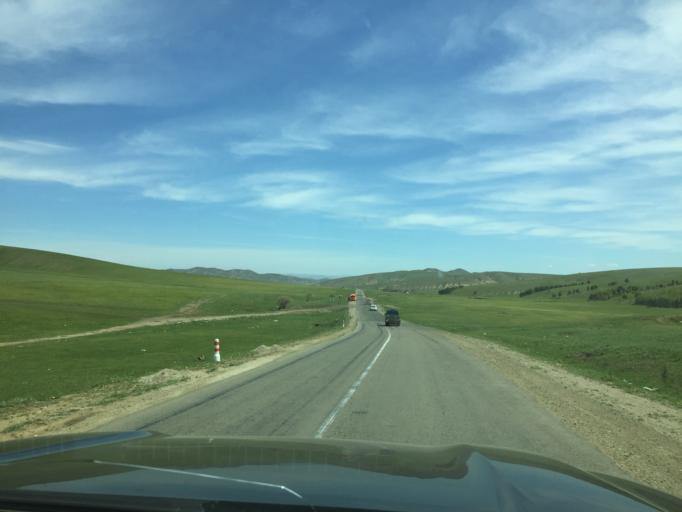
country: MN
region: Central Aimak
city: Javhlant
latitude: 48.6527
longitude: 106.1085
